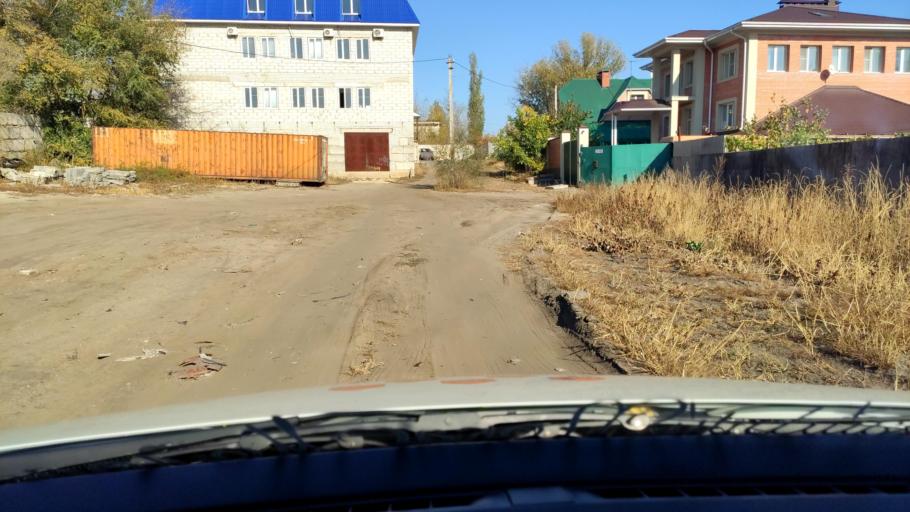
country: RU
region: Voronezj
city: Pridonskoy
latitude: 51.6852
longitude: 39.0646
